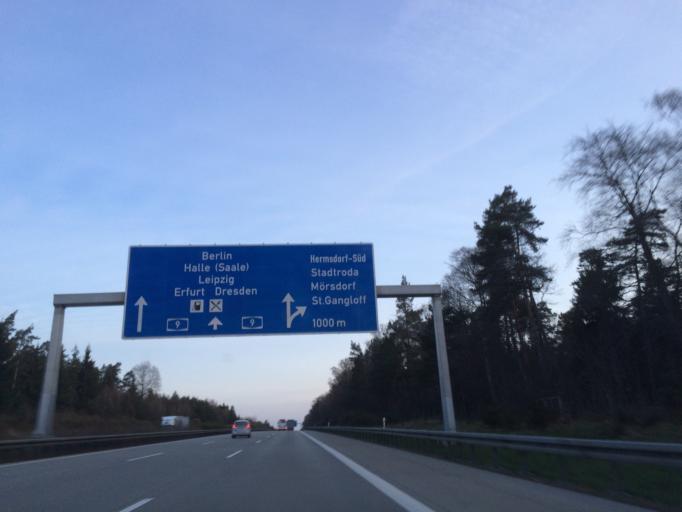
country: DE
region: Thuringia
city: Eineborn
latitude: 50.8503
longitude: 11.8595
